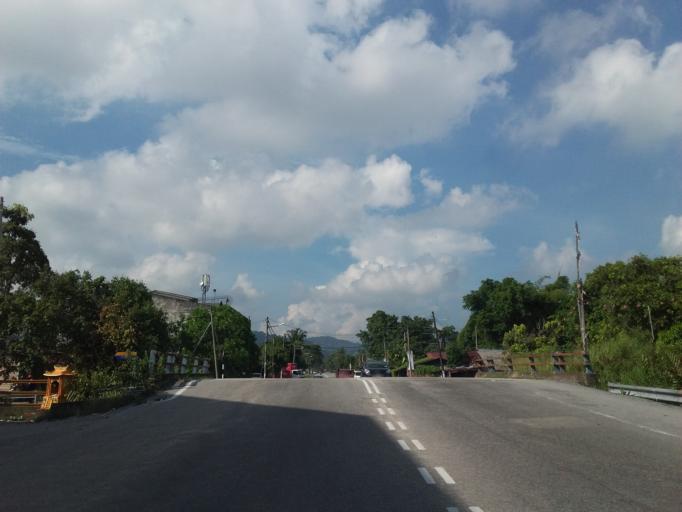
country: MY
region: Johor
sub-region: Daerah Batu Pahat
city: Batu Pahat
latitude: 1.8463
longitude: 102.9248
